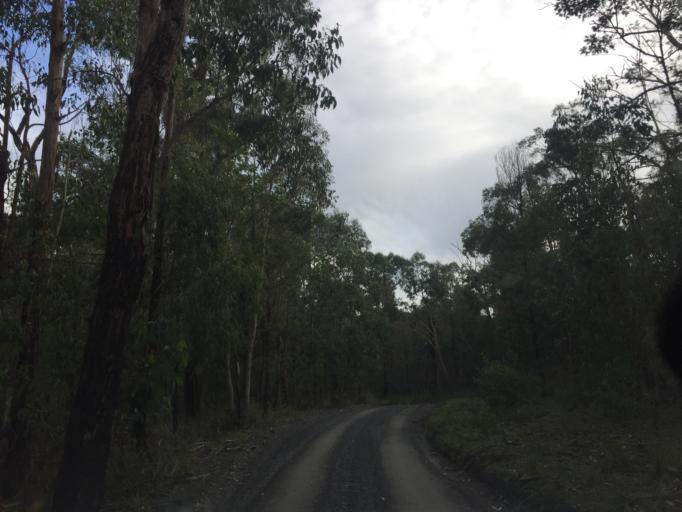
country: AU
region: Victoria
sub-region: Yarra Ranges
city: Healesville
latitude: -37.6155
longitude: 145.4696
